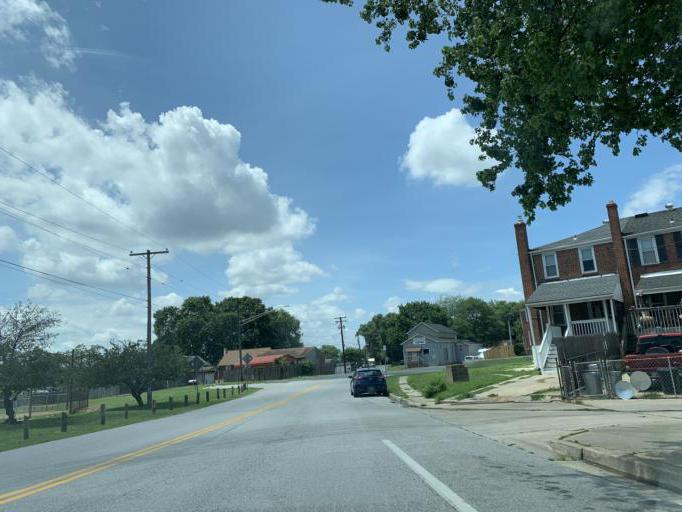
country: US
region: Maryland
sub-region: Baltimore County
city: Edgemere
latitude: 39.2631
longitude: -76.4693
